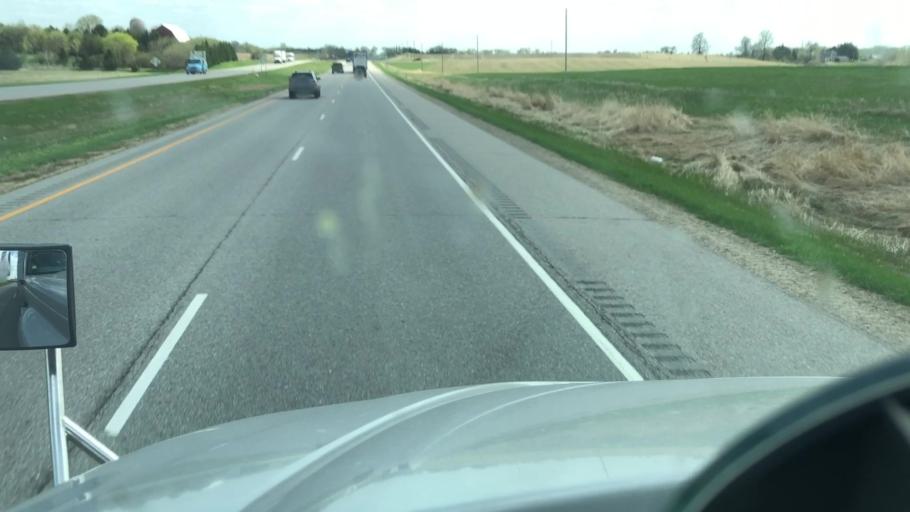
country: US
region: Minnesota
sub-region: Le Sueur County
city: Le Sueur
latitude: 44.5329
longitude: -93.8474
